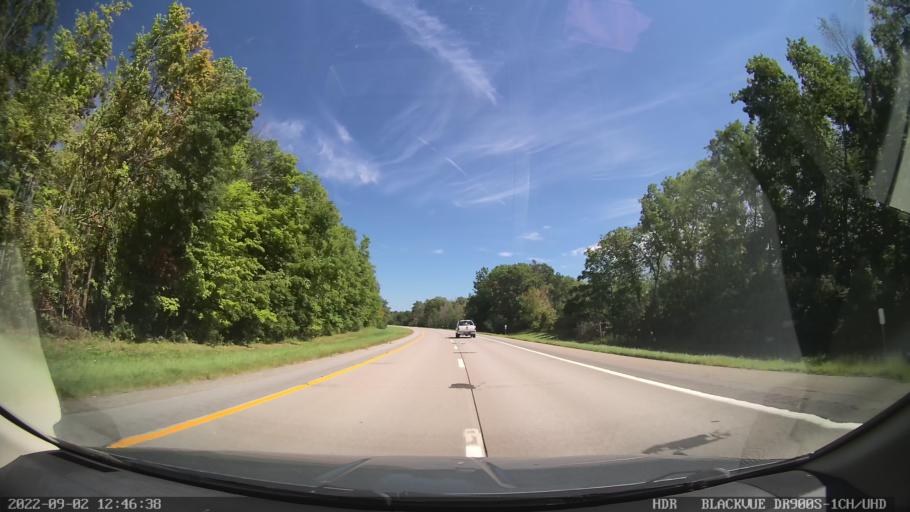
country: US
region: New York
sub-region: Livingston County
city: Geneseo
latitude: 42.8031
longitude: -77.7445
